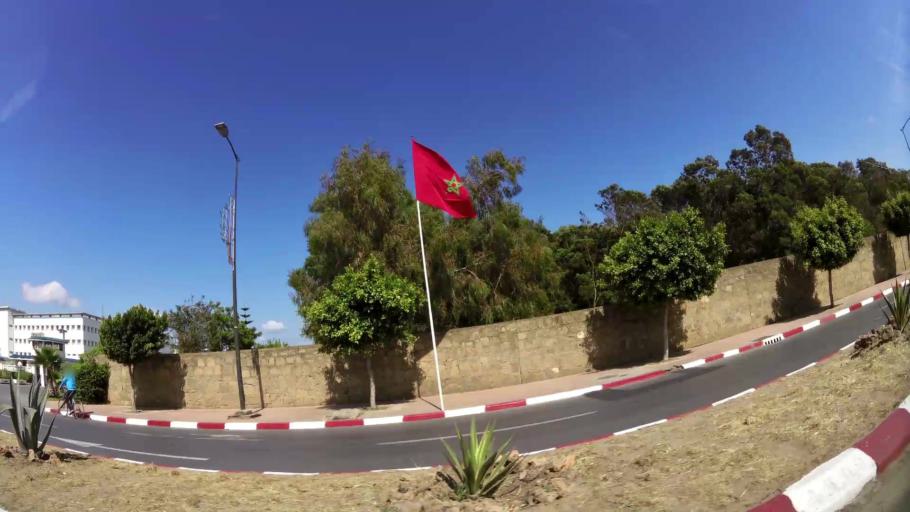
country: MA
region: Rabat-Sale-Zemmour-Zaer
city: Sale
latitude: 34.0449
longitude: -6.7744
